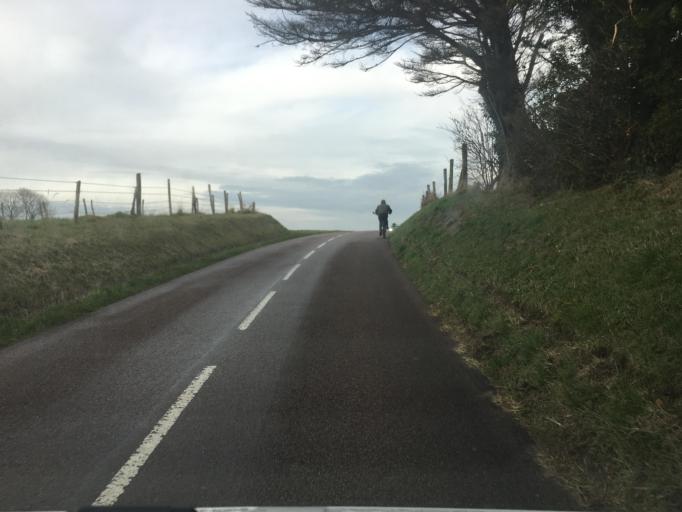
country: FR
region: Lower Normandy
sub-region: Departement du Calvados
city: Ver-sur-Mer
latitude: 49.3333
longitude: -0.6138
